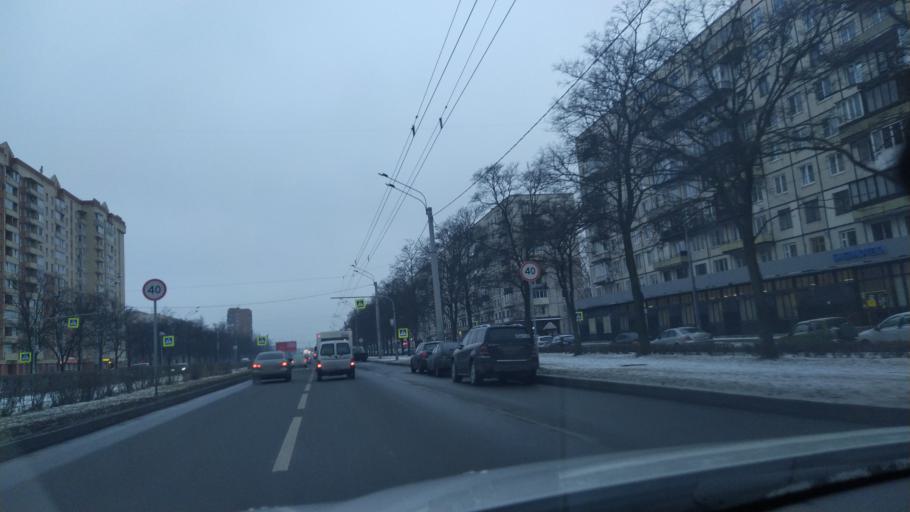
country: RU
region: St.-Petersburg
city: Grazhdanka
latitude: 60.0382
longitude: 30.3974
